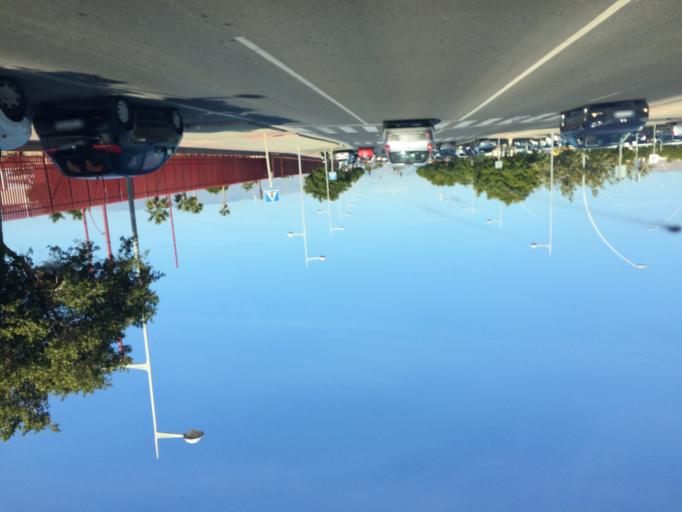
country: ES
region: Andalusia
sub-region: Provincia de Almeria
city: Almeria
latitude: 36.8388
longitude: -2.4323
